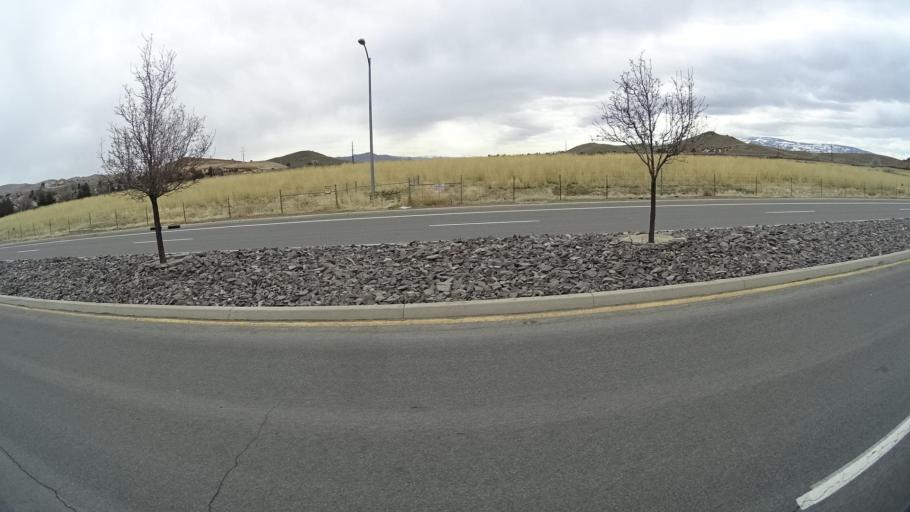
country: US
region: Nevada
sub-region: Washoe County
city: Sparks
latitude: 39.5767
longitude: -119.7266
